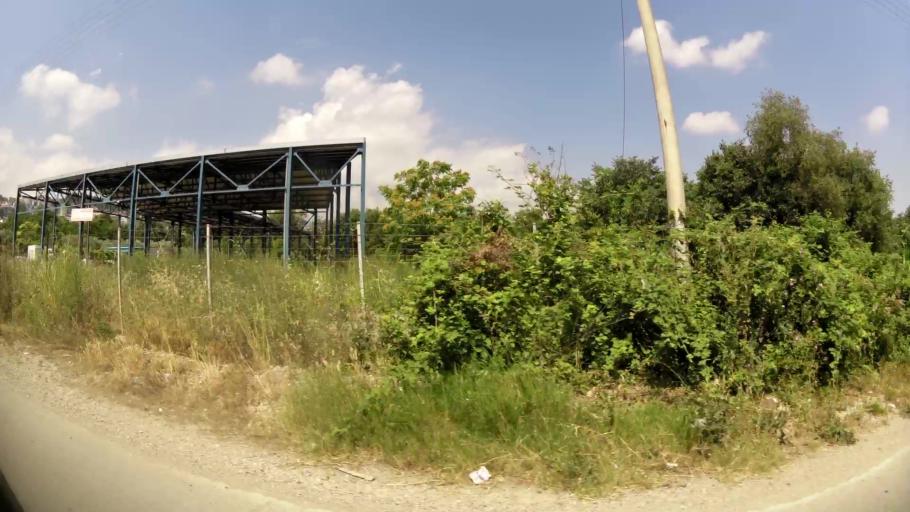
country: GR
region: Central Macedonia
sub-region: Nomos Imathias
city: Veroia
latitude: 40.5190
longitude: 22.2126
